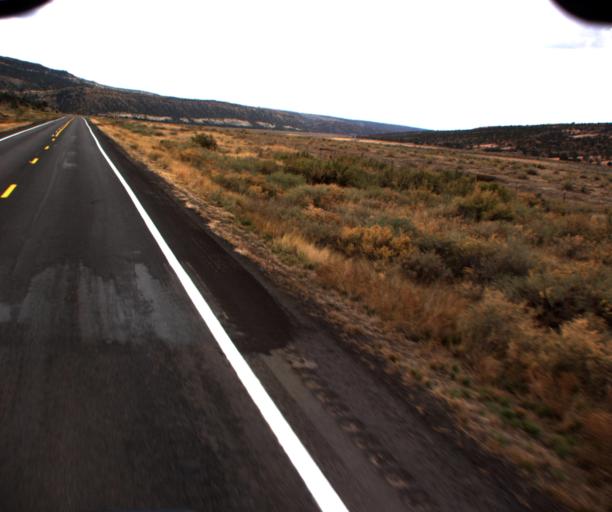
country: US
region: Arizona
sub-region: Navajo County
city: Kayenta
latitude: 36.5975
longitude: -110.4725
